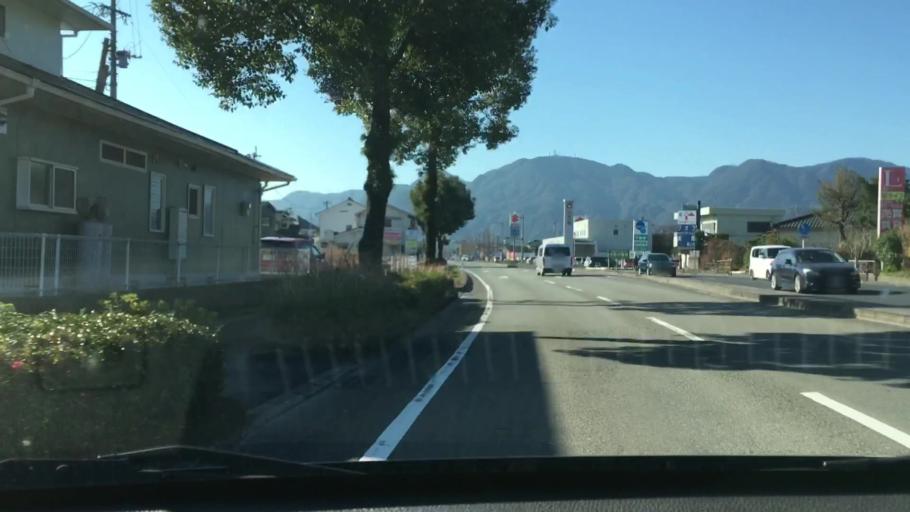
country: JP
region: Kagoshima
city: Kajiki
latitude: 31.7277
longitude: 130.6250
